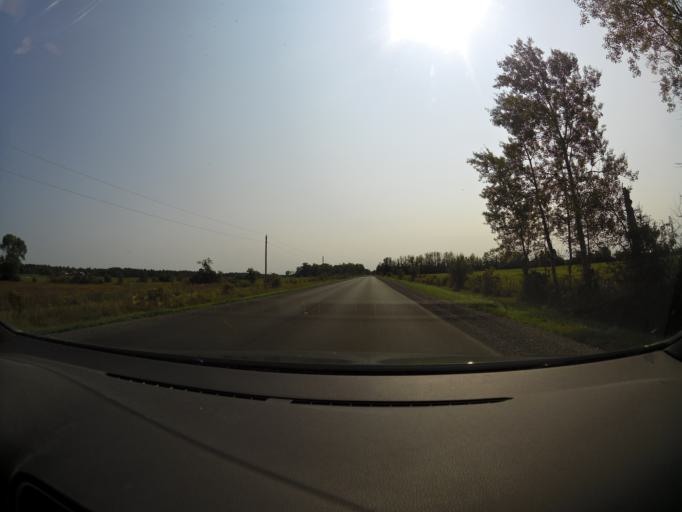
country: CA
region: Ontario
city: Arnprior
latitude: 45.4852
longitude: -76.1863
